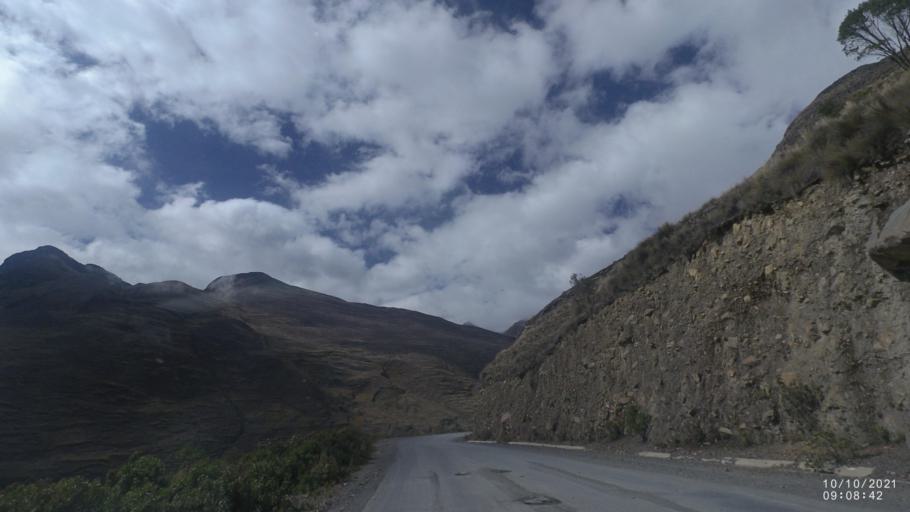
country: BO
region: La Paz
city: Quime
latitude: -17.0172
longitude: -67.2789
